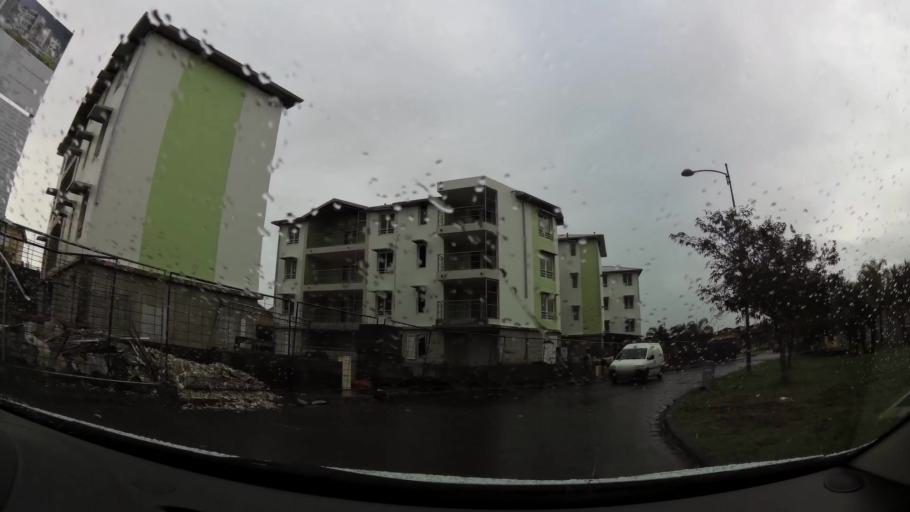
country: RE
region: Reunion
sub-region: Reunion
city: Saint-Andre
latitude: -20.9761
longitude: 55.6489
